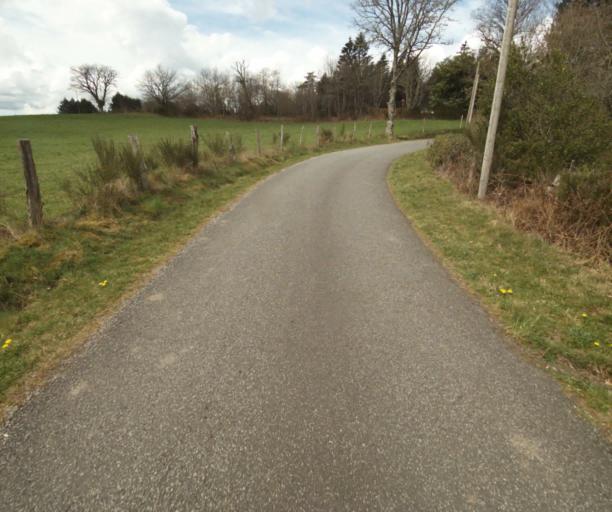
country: FR
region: Limousin
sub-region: Departement de la Correze
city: Correze
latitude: 45.3474
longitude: 1.9376
